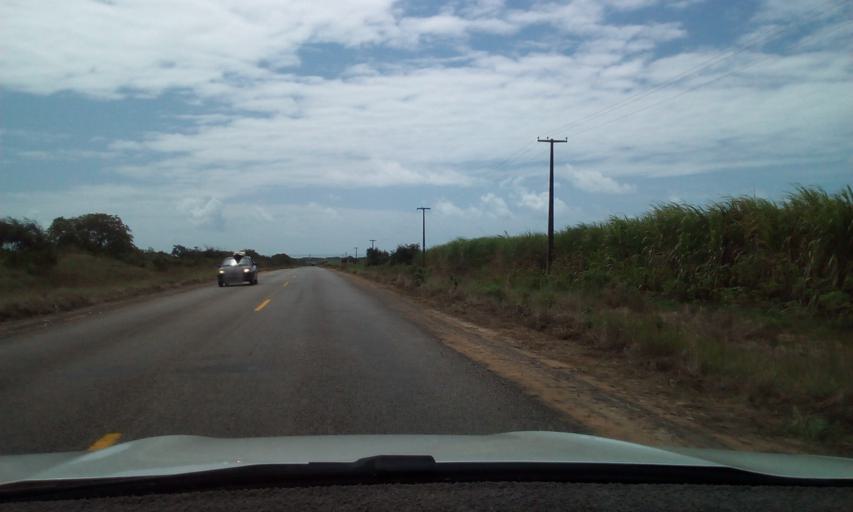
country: BR
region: Paraiba
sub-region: Rio Tinto
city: Rio Tinto
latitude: -6.7454
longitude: -34.9701
